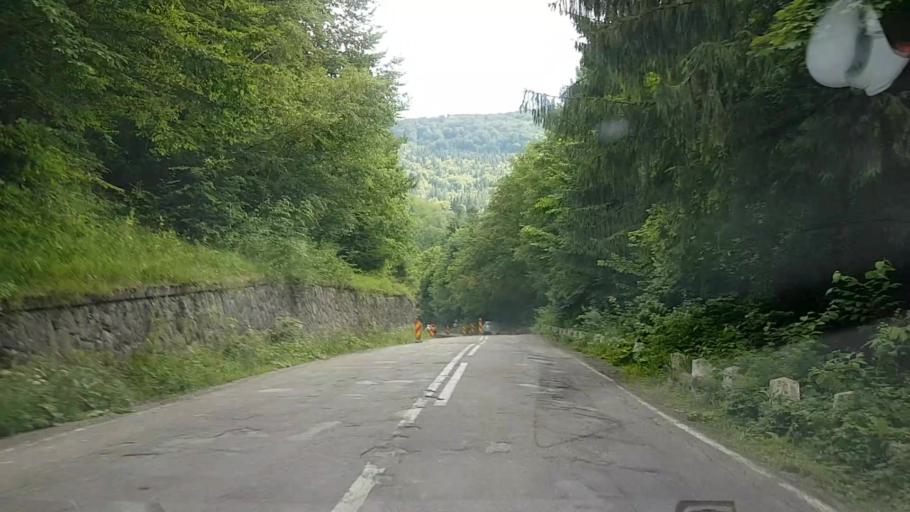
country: RO
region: Neamt
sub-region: Comuna Pangarati
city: Pangarati
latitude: 46.9385
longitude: 26.1274
